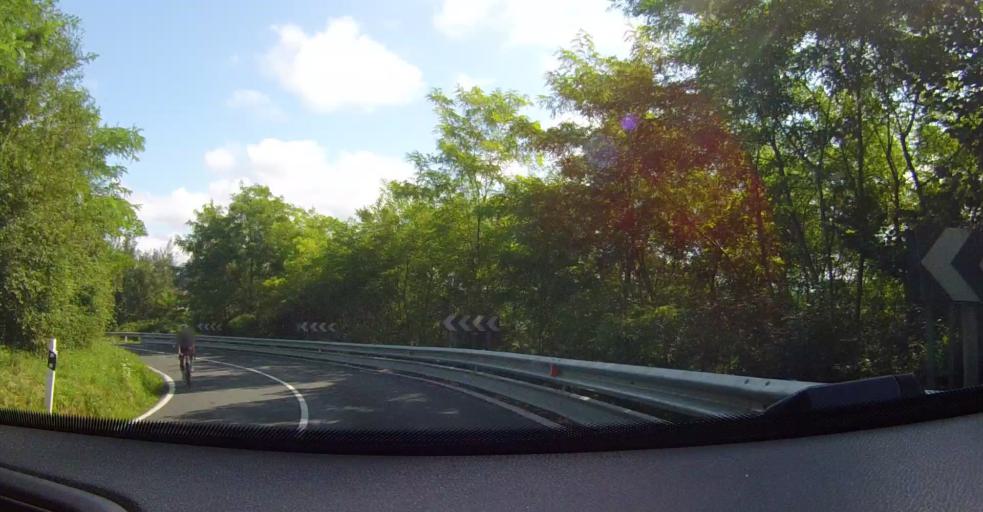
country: ES
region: Basque Country
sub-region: Bizkaia
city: Kortezubi
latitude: 43.3574
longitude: -2.6511
